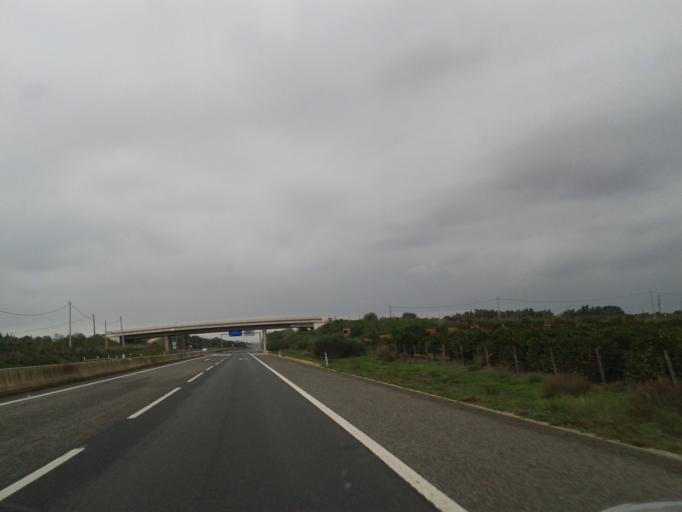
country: PT
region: Faro
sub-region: Lagoa
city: Lagoa
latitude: 37.1515
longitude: -8.4426
